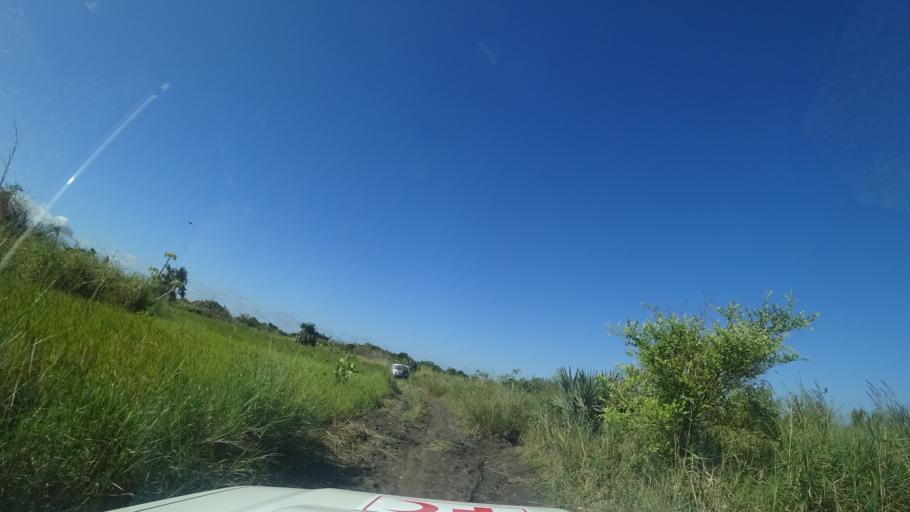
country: MZ
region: Sofala
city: Dondo
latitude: -19.3924
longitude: 34.5918
